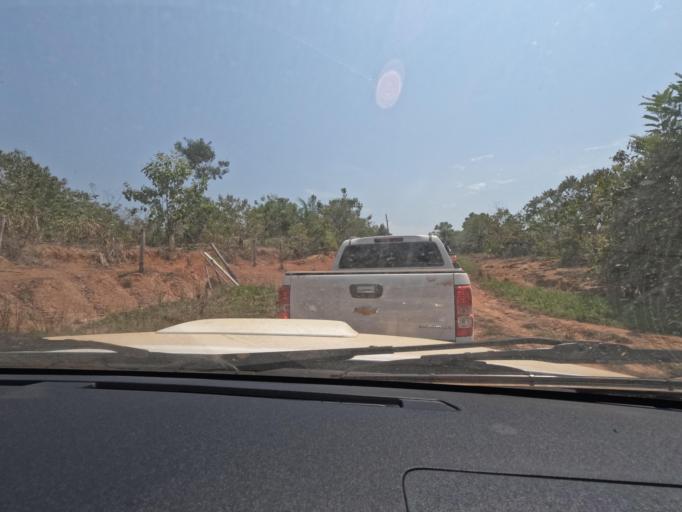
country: BR
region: Rondonia
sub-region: Porto Velho
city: Porto Velho
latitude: -8.6674
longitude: -64.2665
